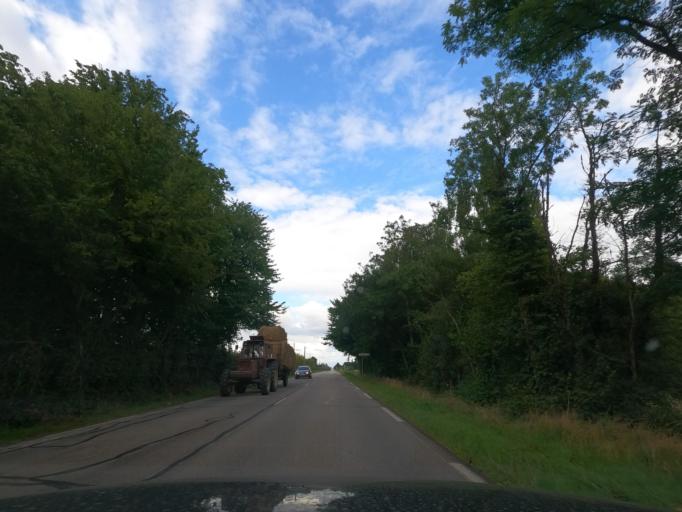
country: FR
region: Lower Normandy
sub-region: Departement du Calvados
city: Orbec
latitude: 48.9054
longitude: 0.4138
